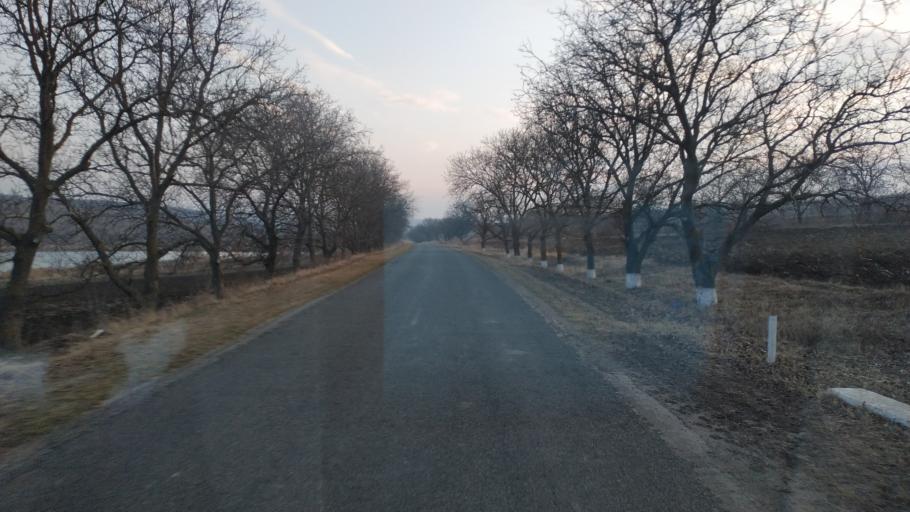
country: MD
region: Hincesti
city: Dancu
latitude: 46.6972
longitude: 28.3366
